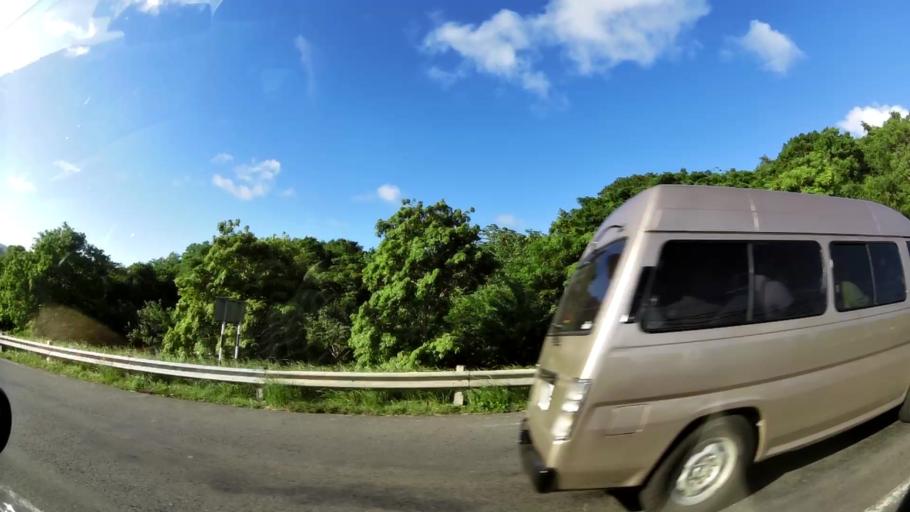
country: TT
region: Tobago
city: Scarborough
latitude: 11.1795
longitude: -60.7062
